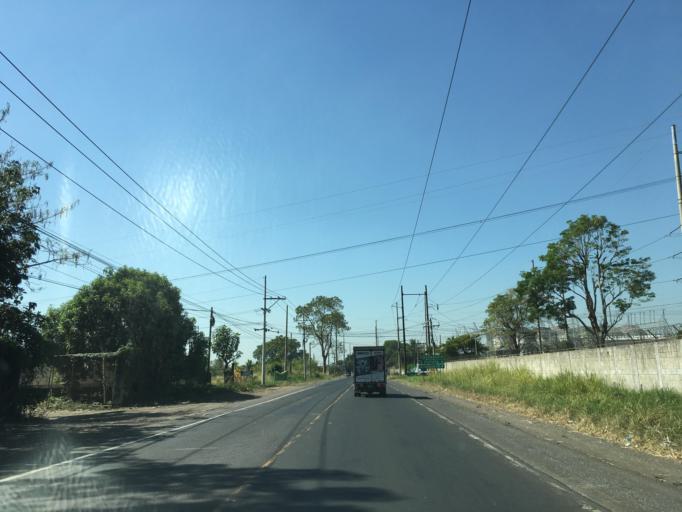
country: GT
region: Escuintla
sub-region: Municipio de Escuintla
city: Escuintla
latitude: 14.2631
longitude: -90.7964
